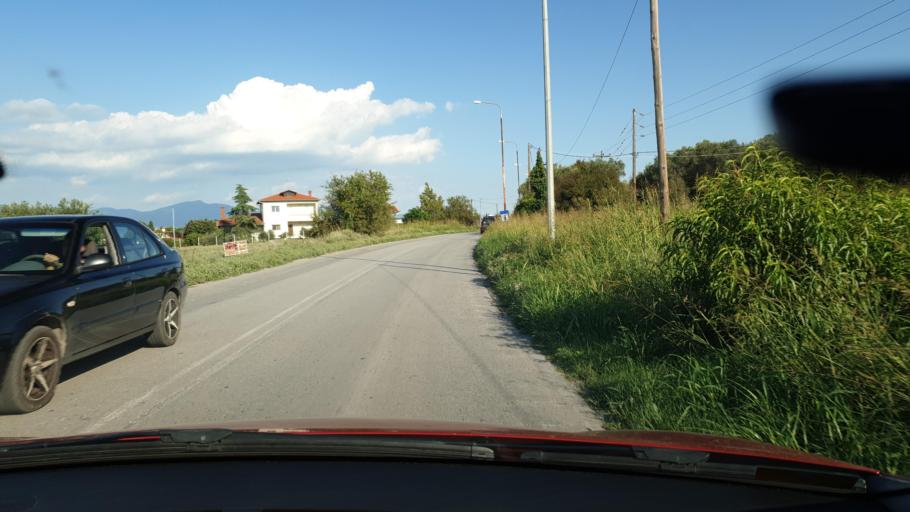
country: GR
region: Central Macedonia
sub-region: Nomos Thessalonikis
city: Neo Rysi
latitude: 40.4940
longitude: 23.0150
